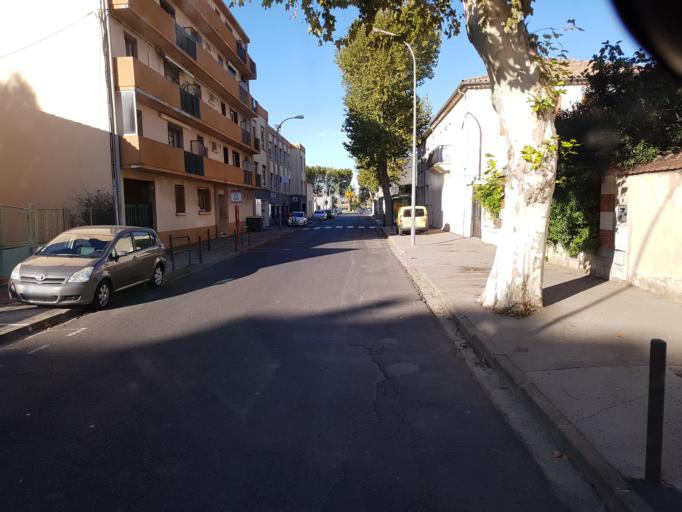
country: FR
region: Languedoc-Roussillon
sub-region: Departement de l'Aude
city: Narbonne
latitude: 43.1920
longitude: 3.0095
